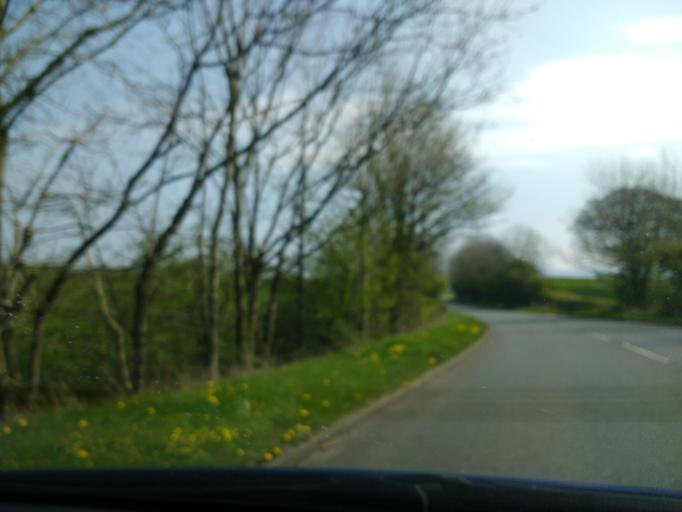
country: GB
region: England
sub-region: Lancashire
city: Bolton le Sands
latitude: 54.0803
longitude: -2.7760
